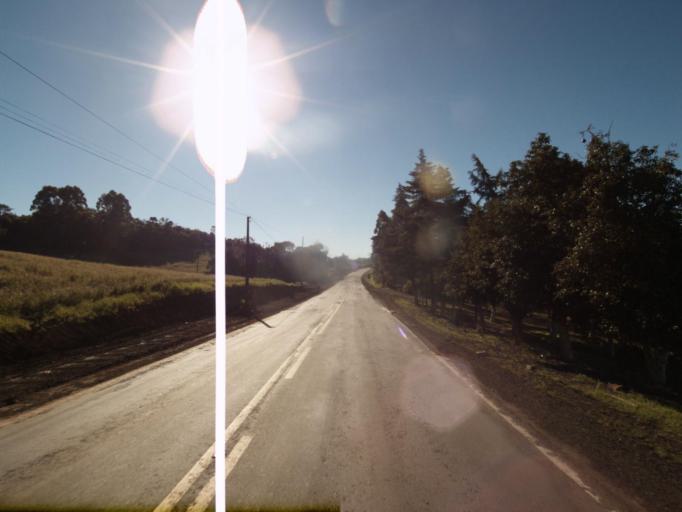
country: AR
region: Misiones
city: Bernardo de Irigoyen
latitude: -26.6202
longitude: -53.5178
